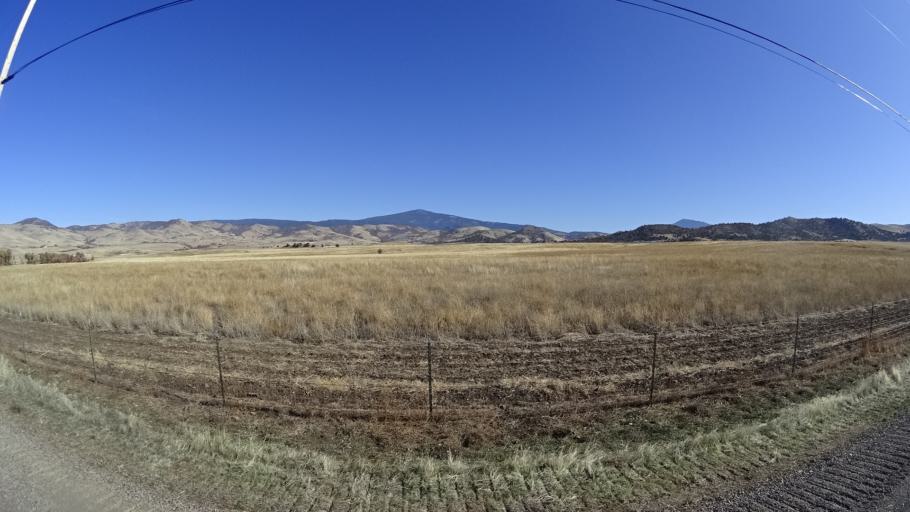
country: US
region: California
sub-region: Siskiyou County
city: Montague
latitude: 41.8073
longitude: -122.4160
